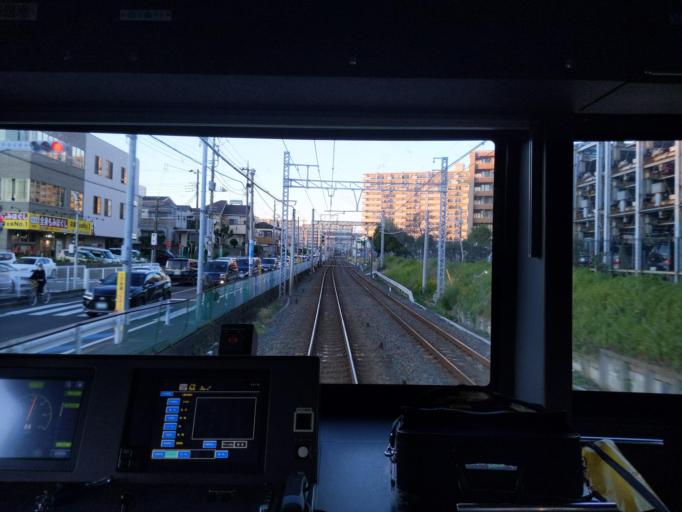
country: JP
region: Chiba
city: Funabashi
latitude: 35.7155
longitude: 139.9804
